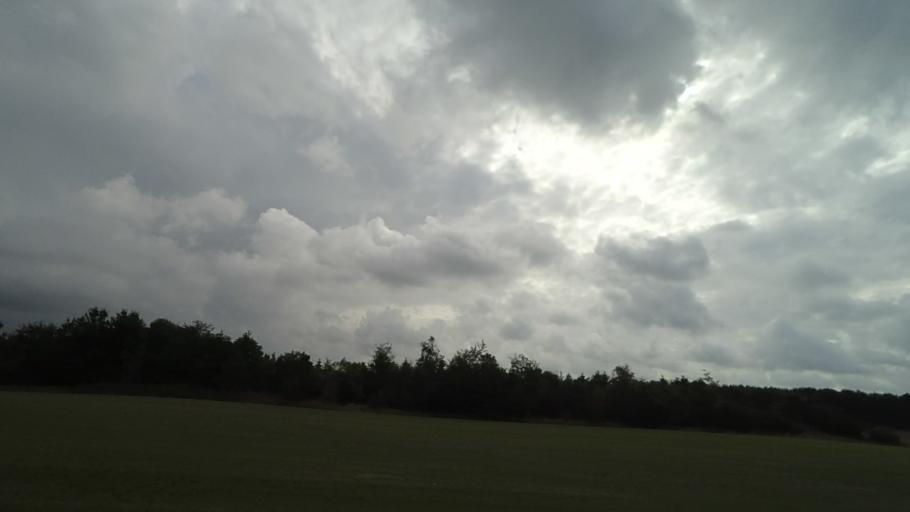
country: DK
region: Central Jutland
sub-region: Syddjurs Kommune
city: Ryomgard
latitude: 56.4228
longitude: 10.5572
